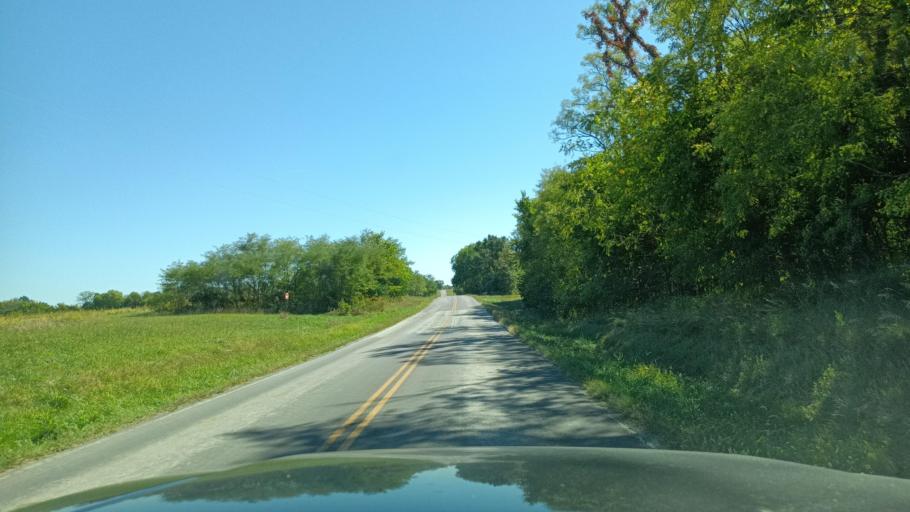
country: US
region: Missouri
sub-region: Macon County
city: La Plata
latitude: 40.0128
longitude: -92.5977
